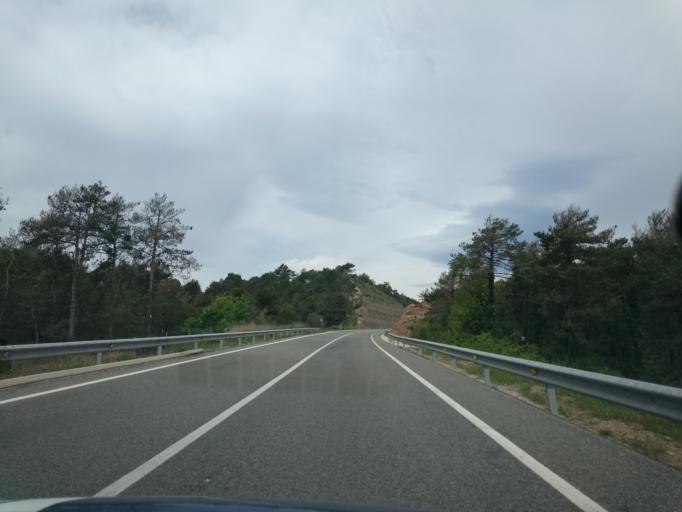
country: ES
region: Catalonia
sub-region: Provincia de Barcelona
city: Olost
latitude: 41.9452
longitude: 2.1391
